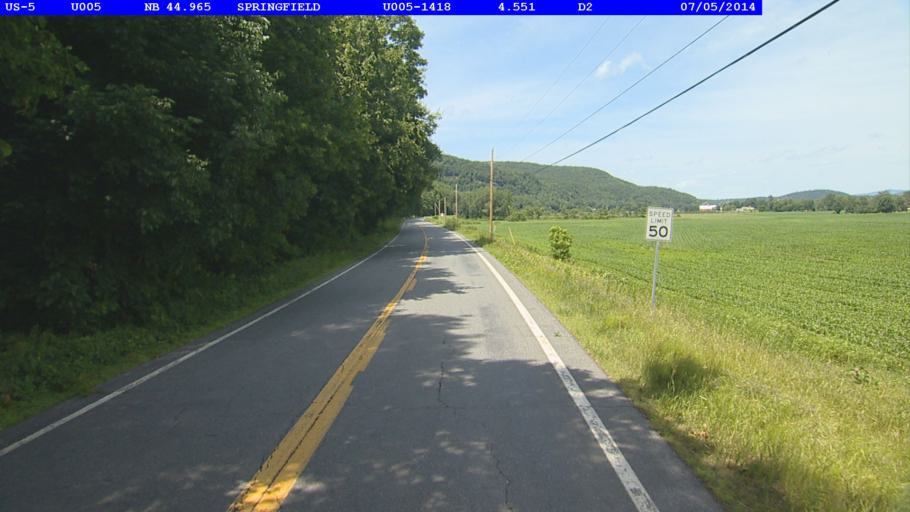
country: US
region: New Hampshire
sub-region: Sullivan County
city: Charlestown
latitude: 43.2794
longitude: -72.4133
